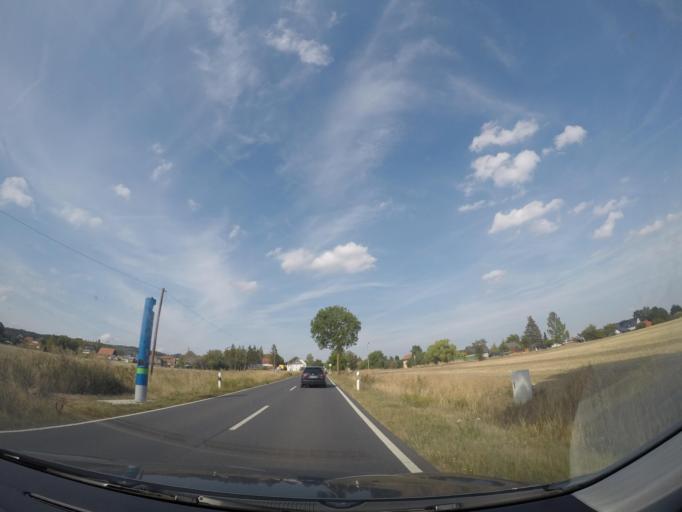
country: DE
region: Lower Saxony
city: Twieflingen
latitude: 52.1244
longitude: 10.9414
